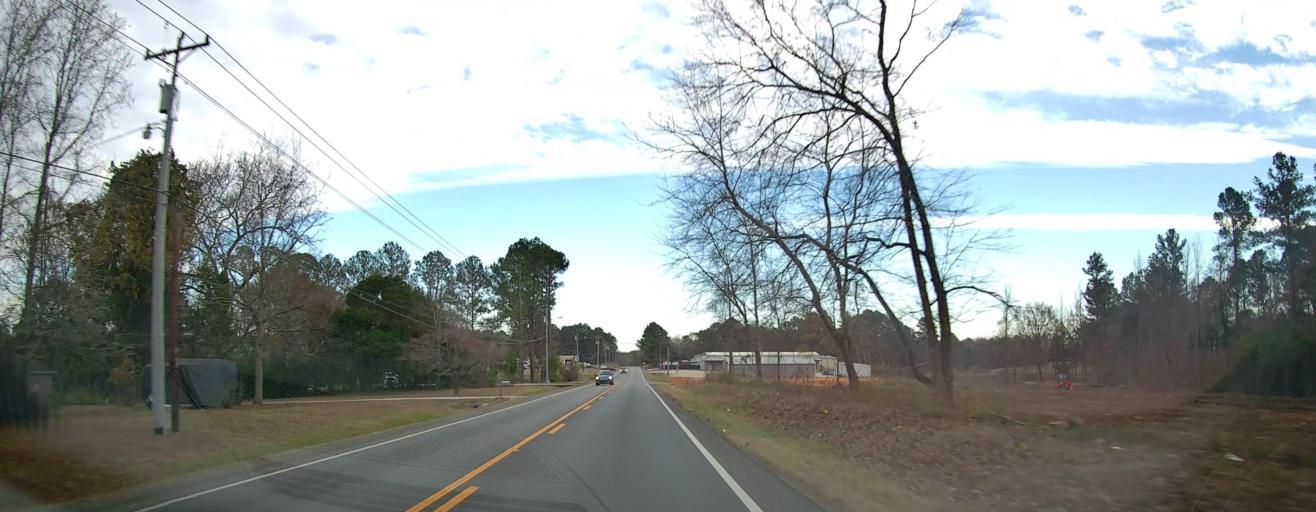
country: US
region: Alabama
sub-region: Morgan County
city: Priceville
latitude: 34.4966
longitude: -86.8480
